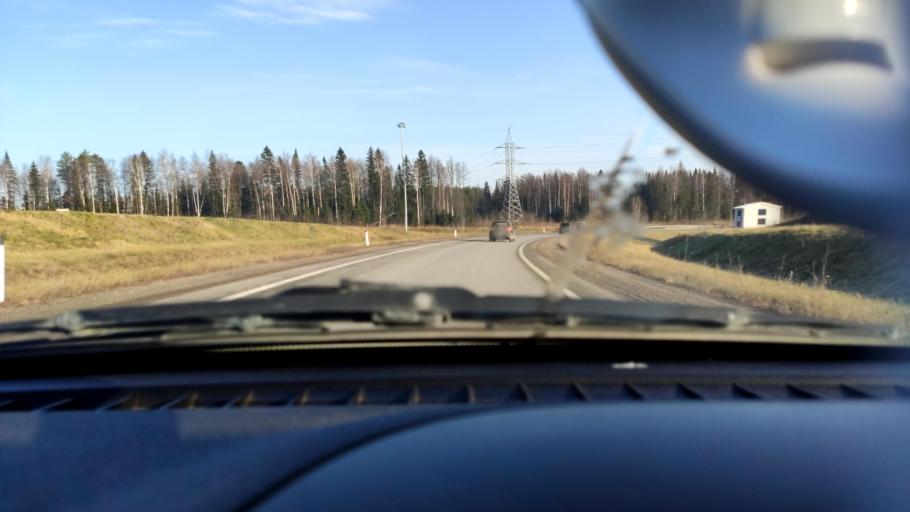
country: RU
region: Perm
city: Novyye Lyady
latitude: 58.0429
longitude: 56.4336
